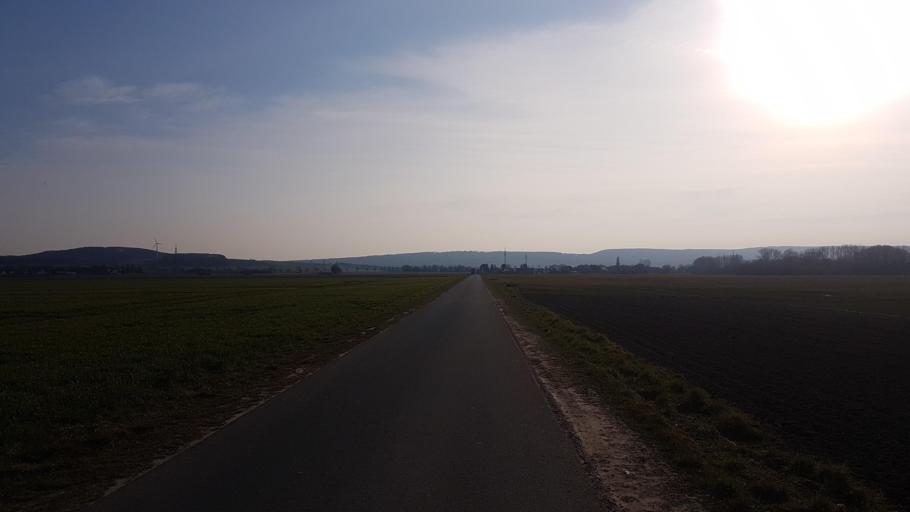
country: DE
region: Lower Saxony
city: Ronnenberg
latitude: 52.2924
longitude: 9.6629
